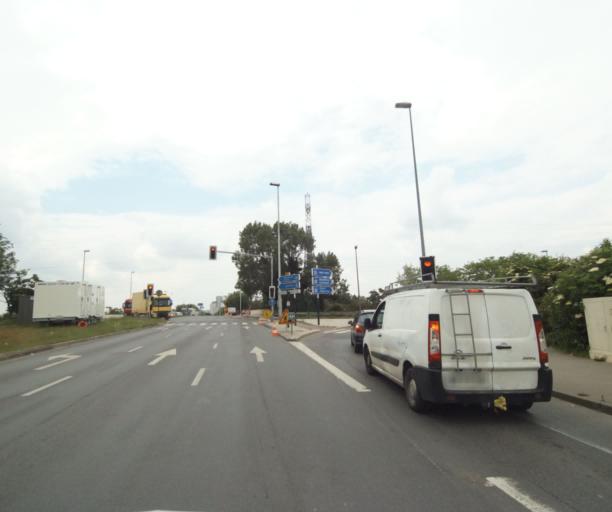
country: FR
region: Ile-de-France
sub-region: Departement des Hauts-de-Seine
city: Bois-Colombes
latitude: 48.9339
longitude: 2.2815
